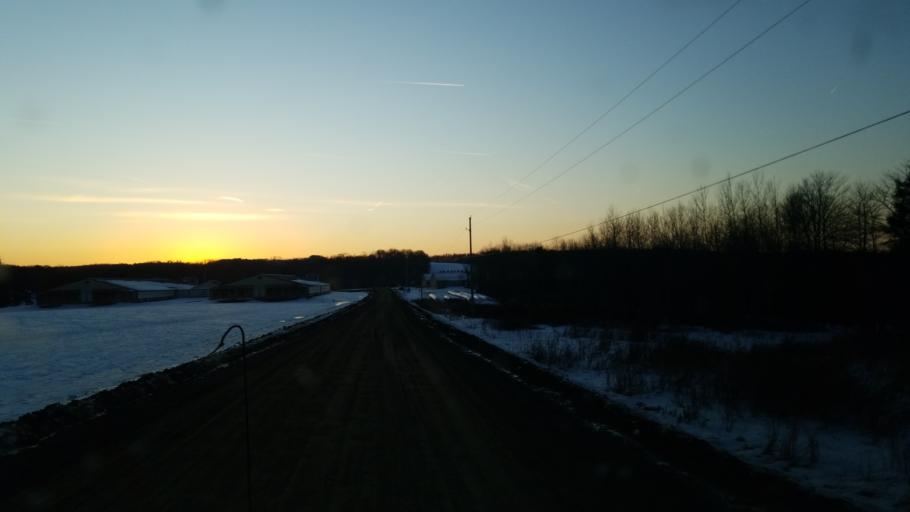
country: US
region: New York
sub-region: Allegany County
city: Andover
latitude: 42.0070
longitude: -77.7158
